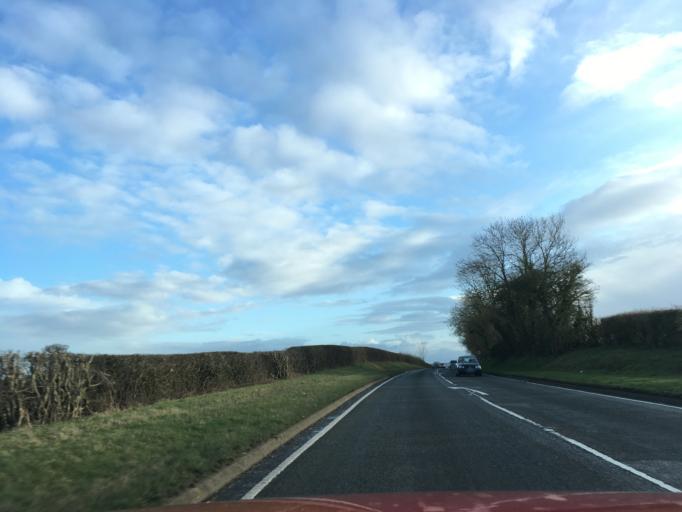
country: GB
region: England
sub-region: Warwickshire
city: Stratford-upon-Avon
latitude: 52.2218
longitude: -1.7340
